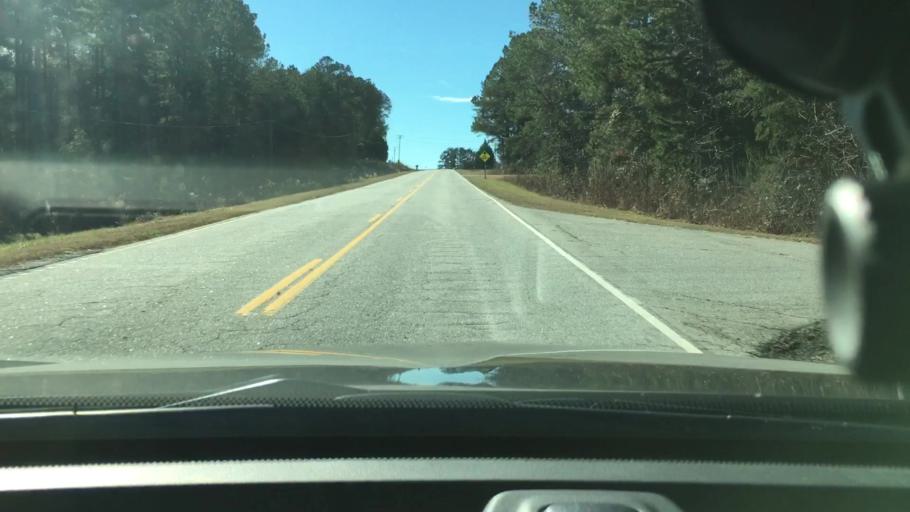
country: US
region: South Carolina
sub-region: Spartanburg County
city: Pacolet
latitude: 34.9563
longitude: -81.7120
